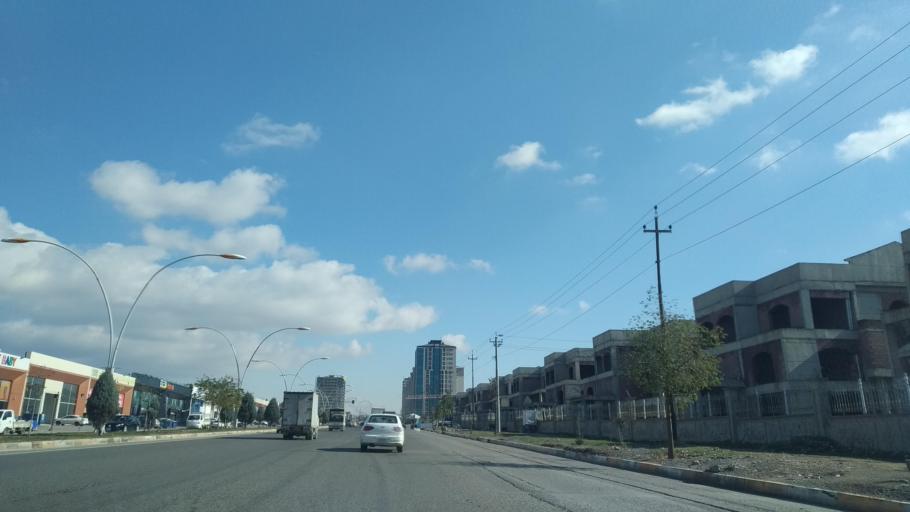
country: IQ
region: Arbil
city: Erbil
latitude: 36.2036
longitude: 44.1116
